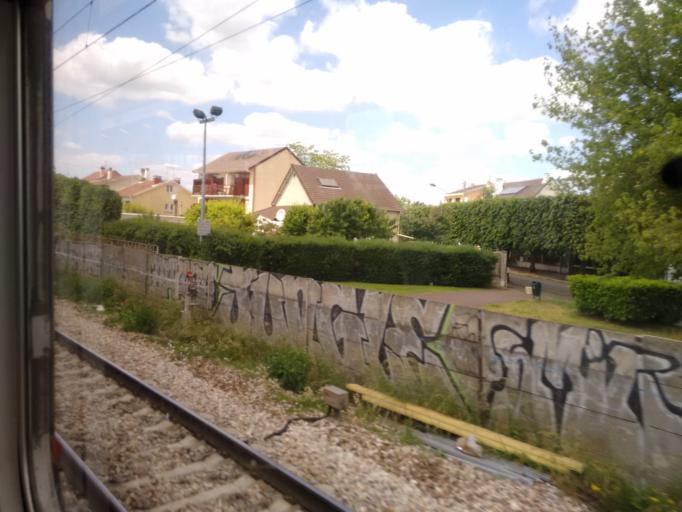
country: FR
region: Ile-de-France
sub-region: Departement de Seine-Saint-Denis
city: Le Blanc-Mesnil
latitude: 48.9325
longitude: 2.4681
